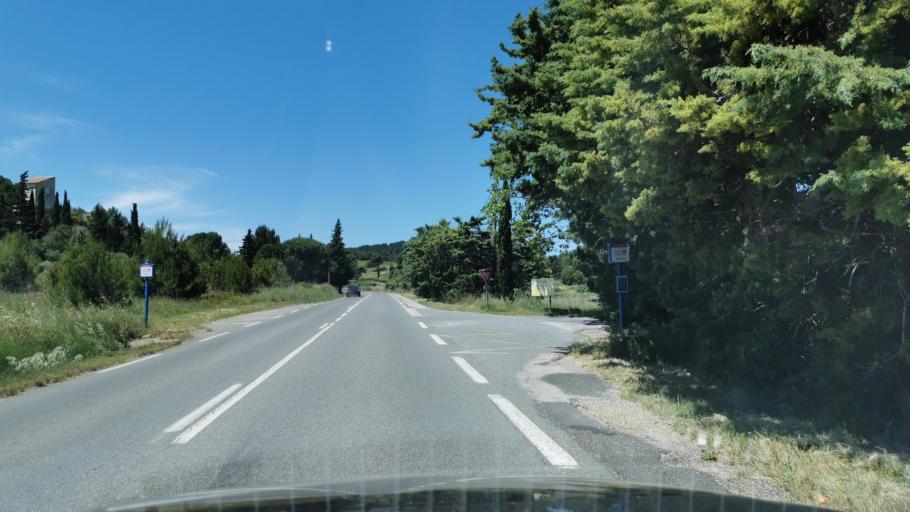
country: FR
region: Languedoc-Roussillon
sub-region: Departement de l'Aude
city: Moussan
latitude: 43.2040
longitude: 2.9637
